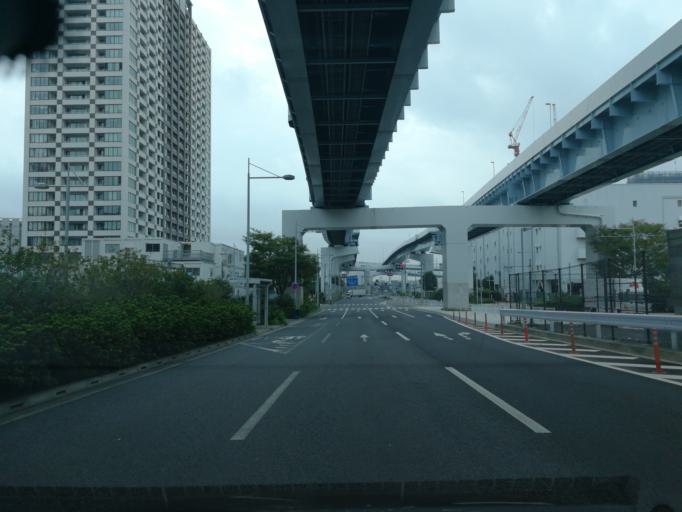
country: JP
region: Tokyo
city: Urayasu
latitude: 35.6427
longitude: 139.7935
